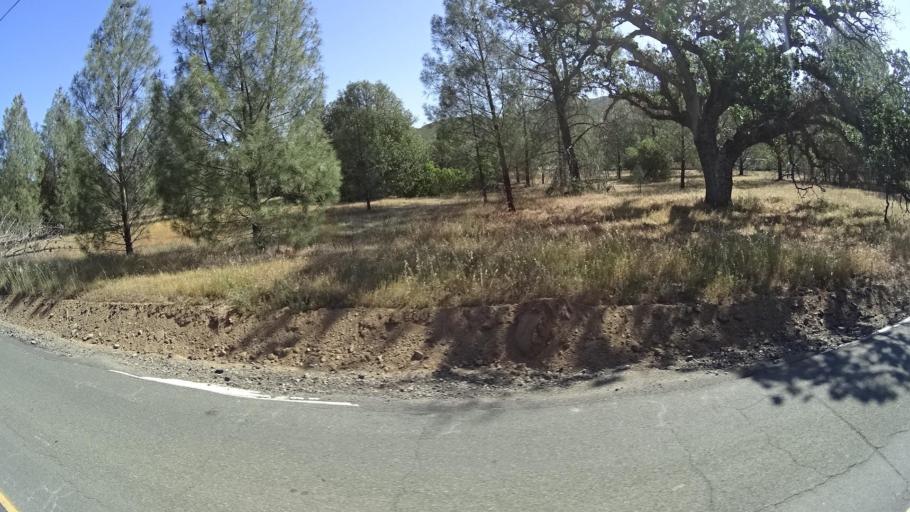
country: US
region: California
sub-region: Lake County
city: Clearlake Oaks
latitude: 39.0517
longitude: -122.5843
